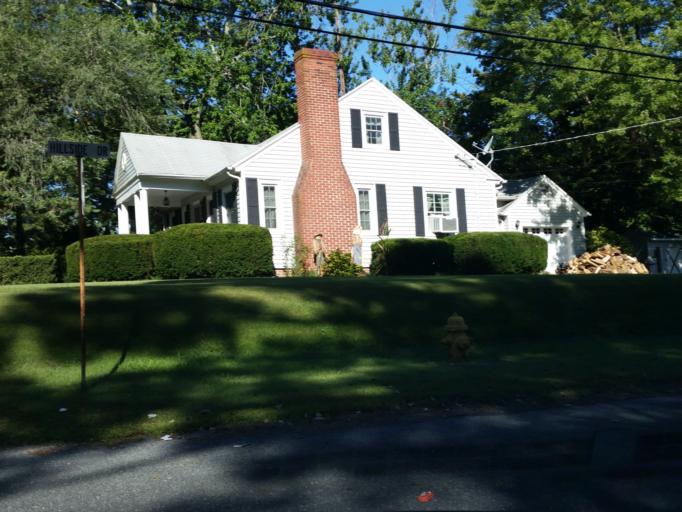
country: US
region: Maryland
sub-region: Wicomico County
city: Salisbury
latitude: 38.3622
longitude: -75.5821
